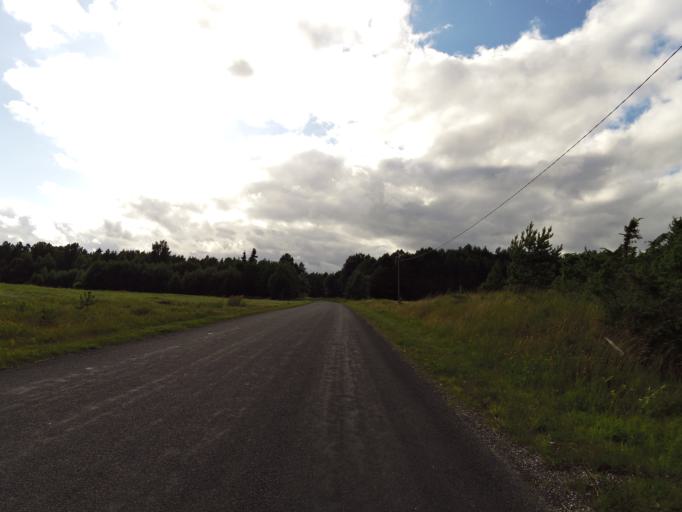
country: EE
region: Laeaene
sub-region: Vormsi vald
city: Hullo
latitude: 58.9848
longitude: 23.2952
